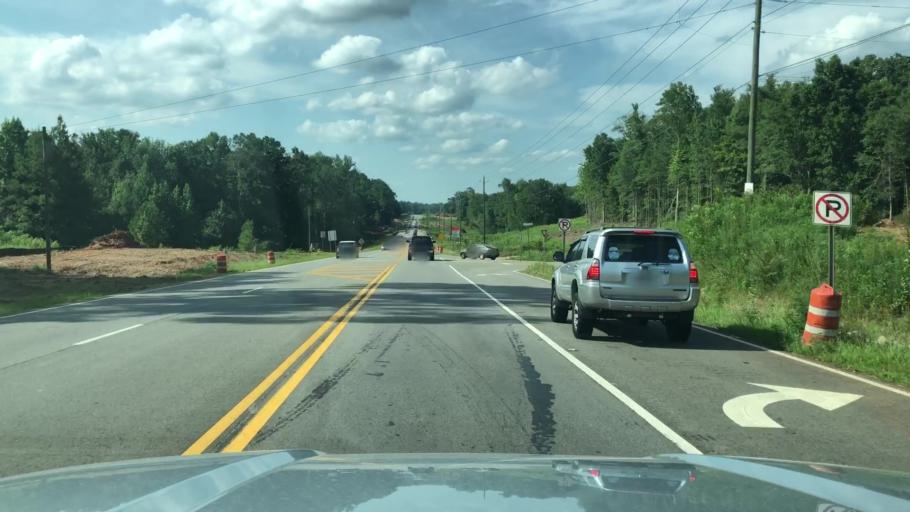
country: US
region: Georgia
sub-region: Paulding County
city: Hiram
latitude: 33.8153
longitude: -84.7583
